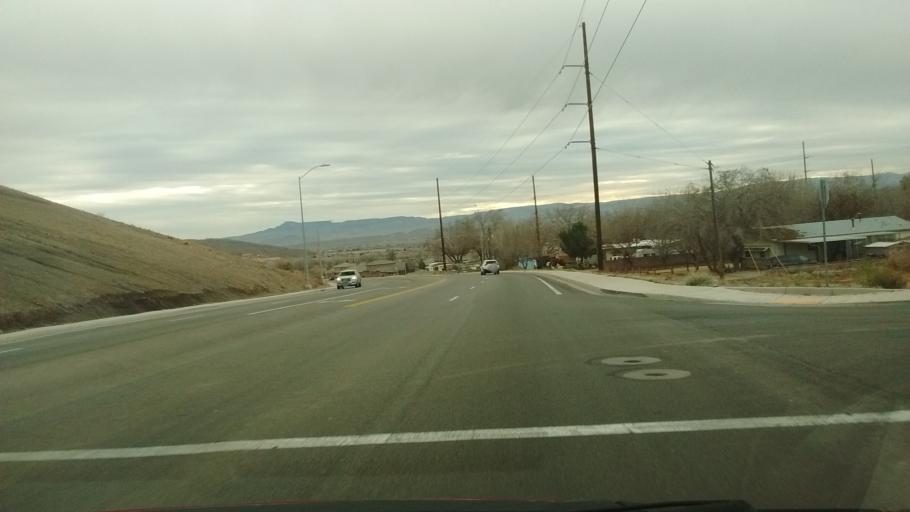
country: US
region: Utah
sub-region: Washington County
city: Washington
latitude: 37.1265
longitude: -113.5052
